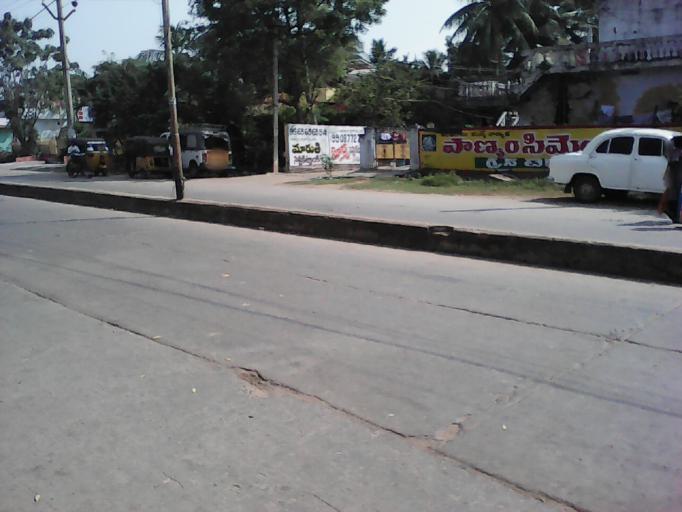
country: IN
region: Andhra Pradesh
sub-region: Guntur
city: Bhattiprolu
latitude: 16.2380
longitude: 80.6585
